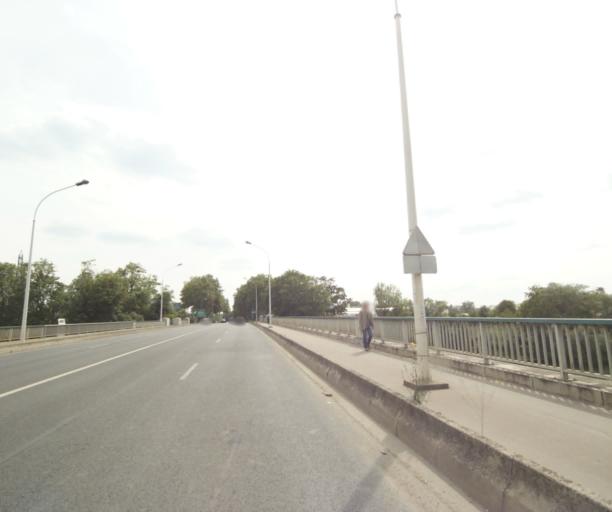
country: FR
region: Ile-de-France
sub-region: Departement de Seine-Saint-Denis
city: Epinay-sur-Seine
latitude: 48.9495
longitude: 2.3064
